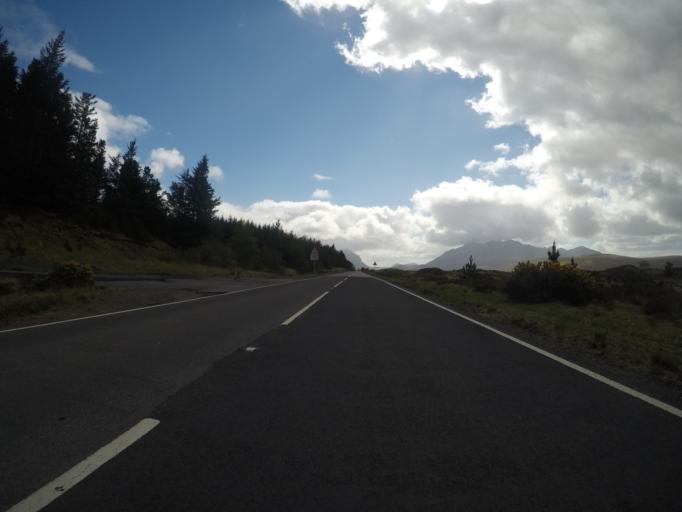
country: GB
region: Scotland
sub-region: Highland
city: Isle of Skye
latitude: 57.3202
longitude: -6.2046
